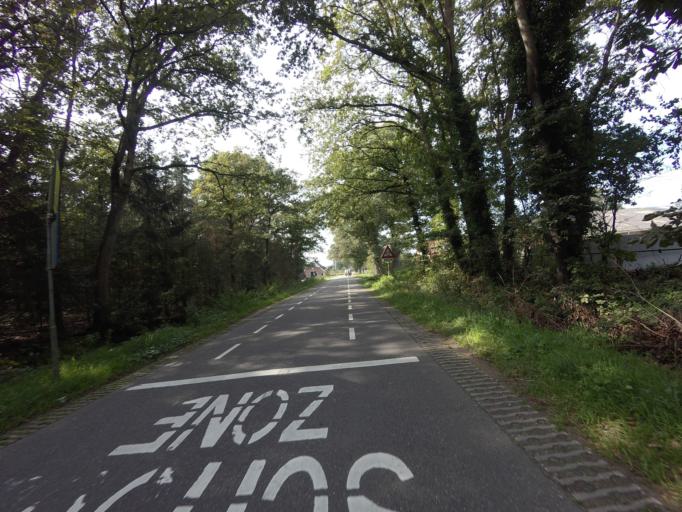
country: NL
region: Overijssel
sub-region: Gemeente Hof van Twente
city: Markelo
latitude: 52.2583
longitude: 6.5324
